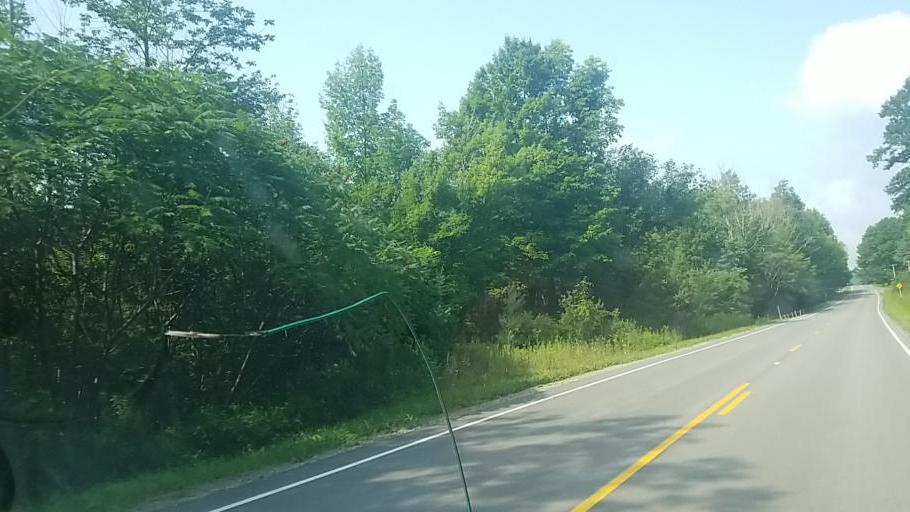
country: US
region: New York
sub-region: Fulton County
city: Gloversville
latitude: 43.1025
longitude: -74.3034
